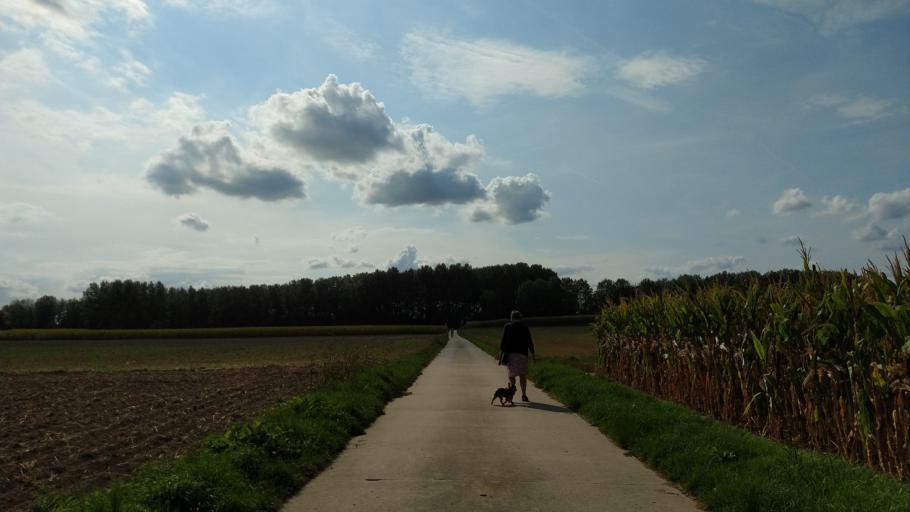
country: BE
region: Flanders
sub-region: Provincie Vlaams-Brabant
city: Boutersem
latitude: 50.8320
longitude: 4.8510
